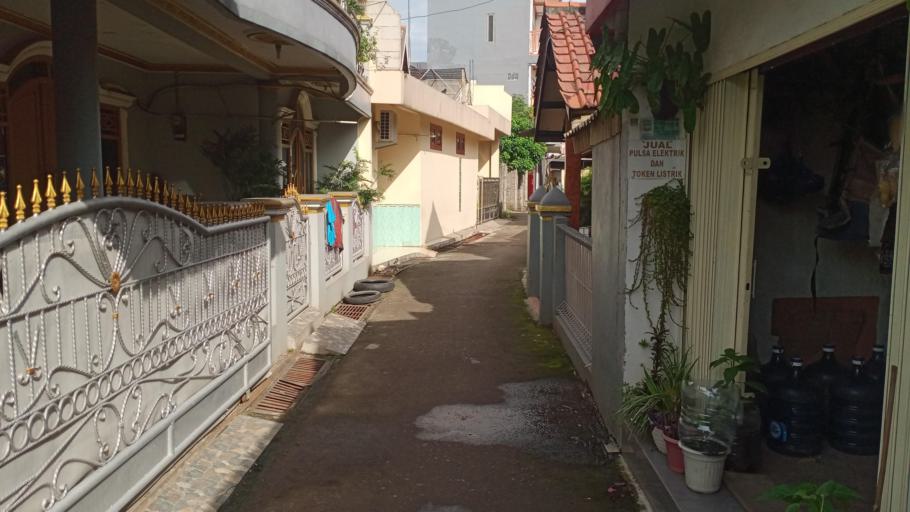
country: ID
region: West Java
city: Cikarang
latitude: -6.2641
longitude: 107.1159
